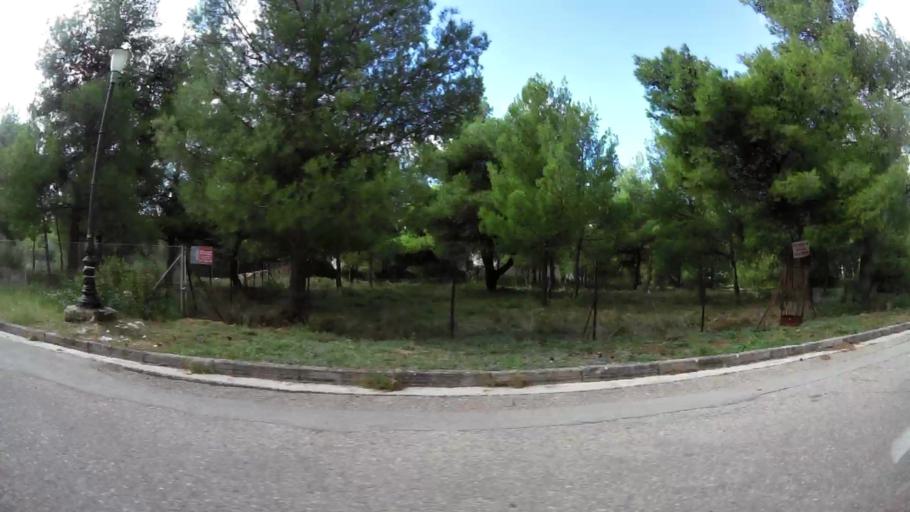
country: GR
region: Attica
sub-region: Nomarchia Anatolikis Attikis
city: Thrakomakedones
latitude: 38.1254
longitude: 23.7602
